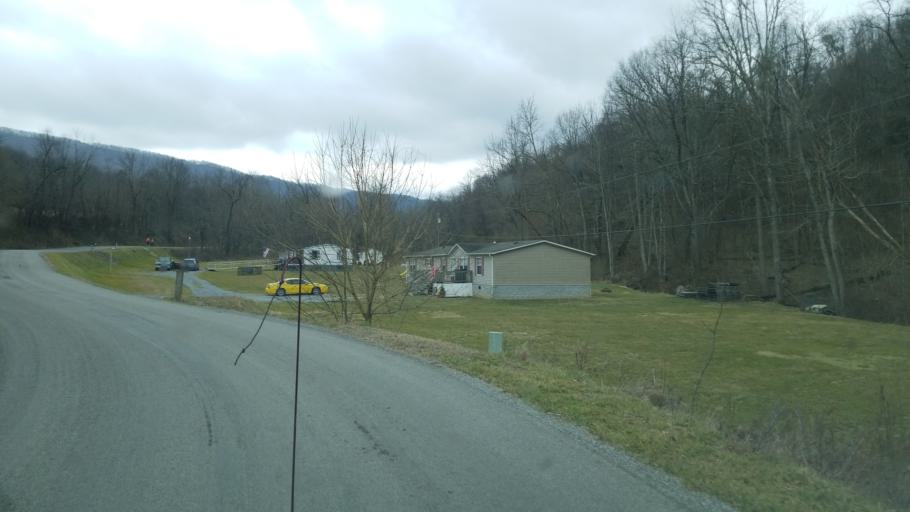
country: US
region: Virginia
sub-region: Giles County
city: Pembroke
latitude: 37.2429
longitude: -80.6771
